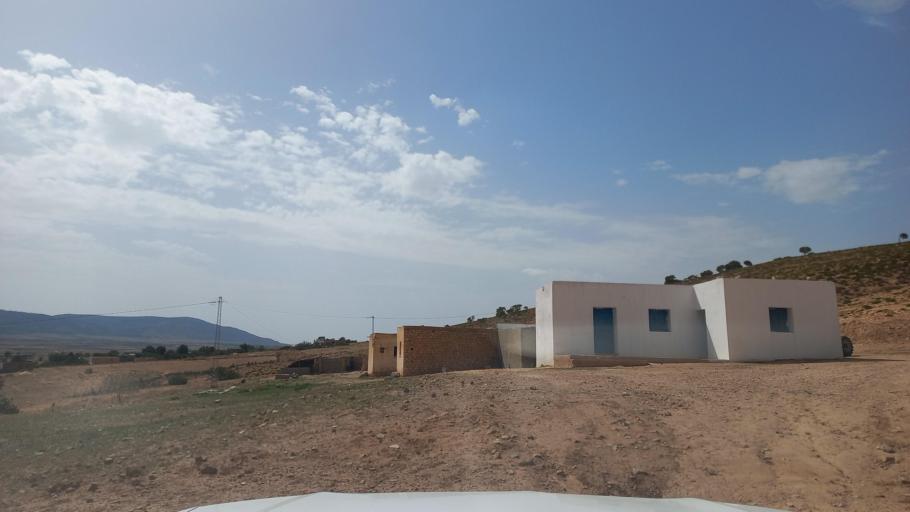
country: TN
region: Al Qasrayn
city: Kasserine
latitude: 35.3728
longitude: 8.8781
